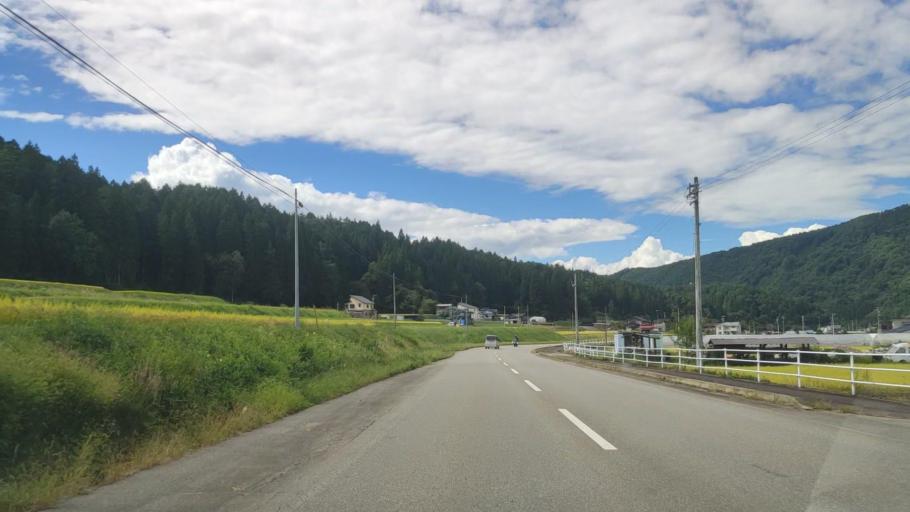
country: JP
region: Gifu
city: Takayama
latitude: 36.1750
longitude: 137.2880
